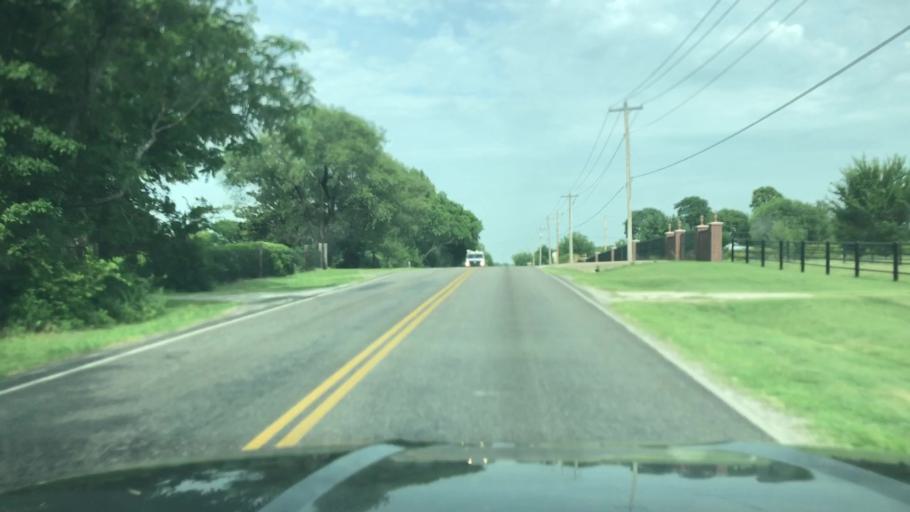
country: US
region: Oklahoma
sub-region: Tulsa County
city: Oakhurst
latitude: 36.0902
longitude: -96.0936
